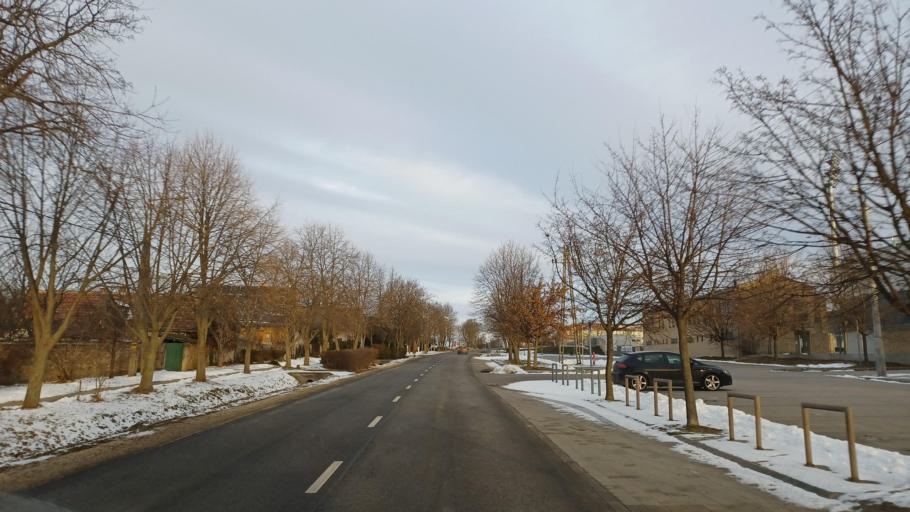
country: HU
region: Tolna
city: Paks
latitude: 46.6329
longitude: 18.8516
